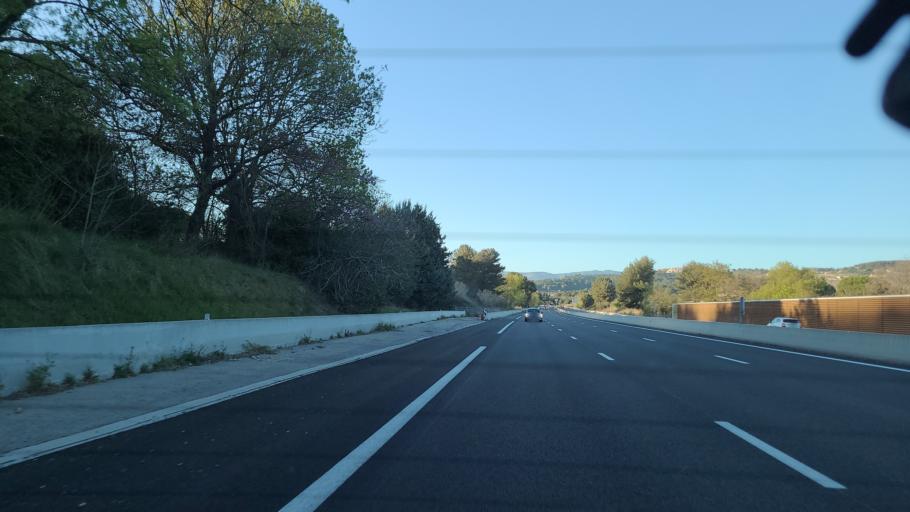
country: FR
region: Provence-Alpes-Cote d'Azur
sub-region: Departement du Var
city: Le Castellet
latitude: 43.1755
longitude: 5.7696
